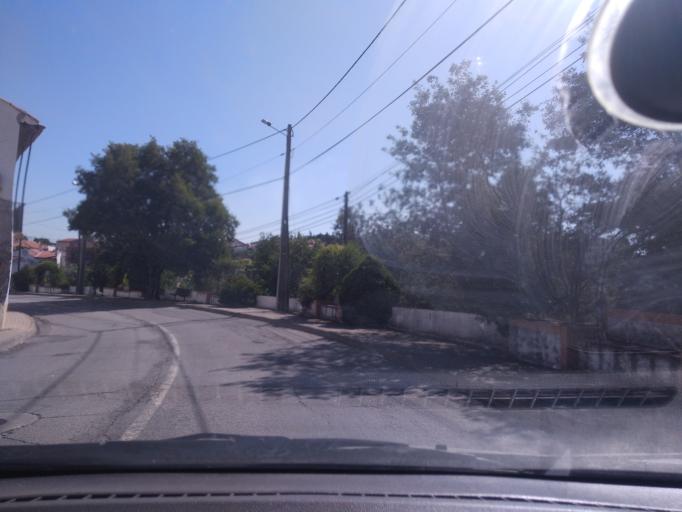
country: PT
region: Portalegre
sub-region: Nisa
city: Nisa
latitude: 39.6530
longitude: -7.6700
